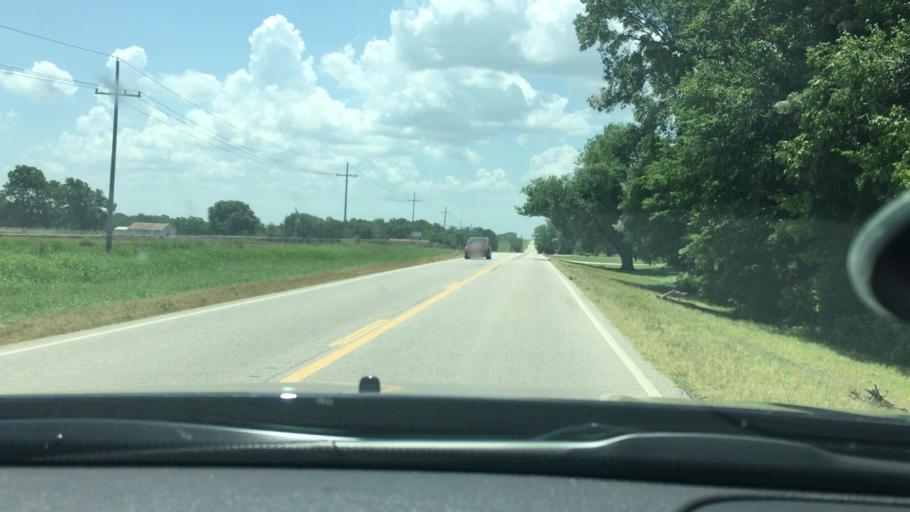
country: US
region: Oklahoma
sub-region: Pontotoc County
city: Ada
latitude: 34.6915
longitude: -96.6349
